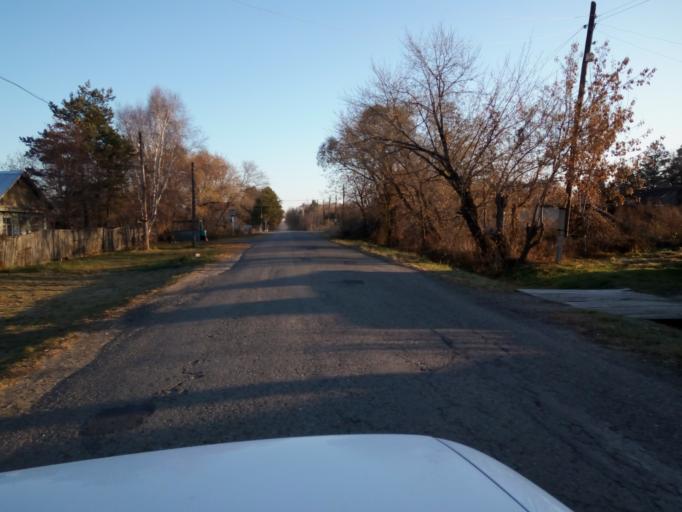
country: RU
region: Primorskiy
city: Lazo
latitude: 45.8741
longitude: 133.6489
